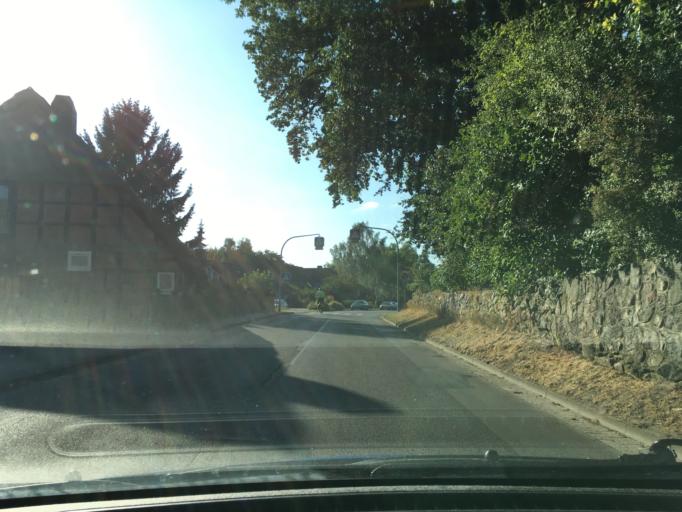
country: DE
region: Lower Saxony
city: Bienenbuttel
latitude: 53.1356
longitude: 10.5069
